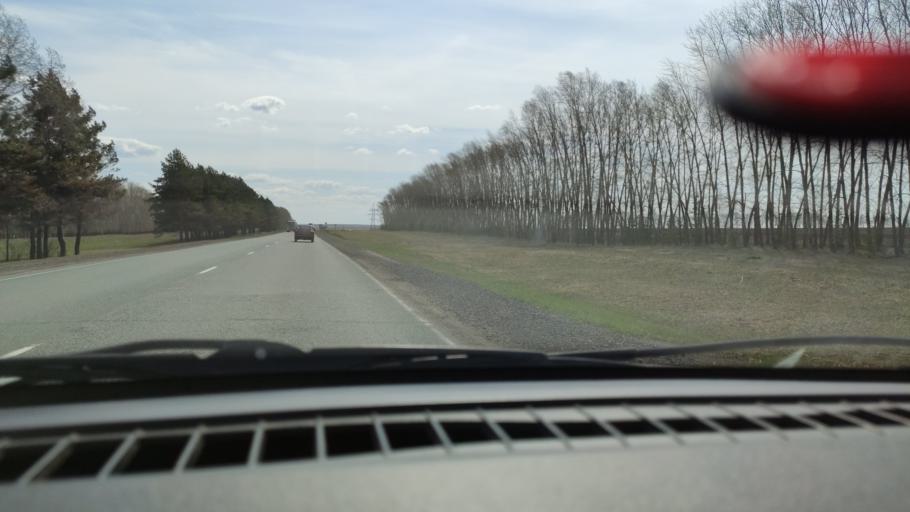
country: RU
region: Bashkortostan
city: Kushnarenkovo
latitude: 55.1803
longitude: 55.1280
